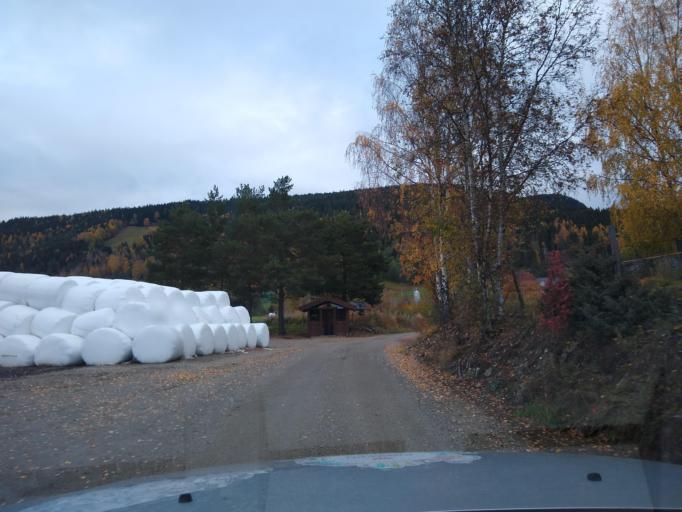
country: NO
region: Oppland
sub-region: Ringebu
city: Ringebu
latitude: 61.5441
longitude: 10.1209
